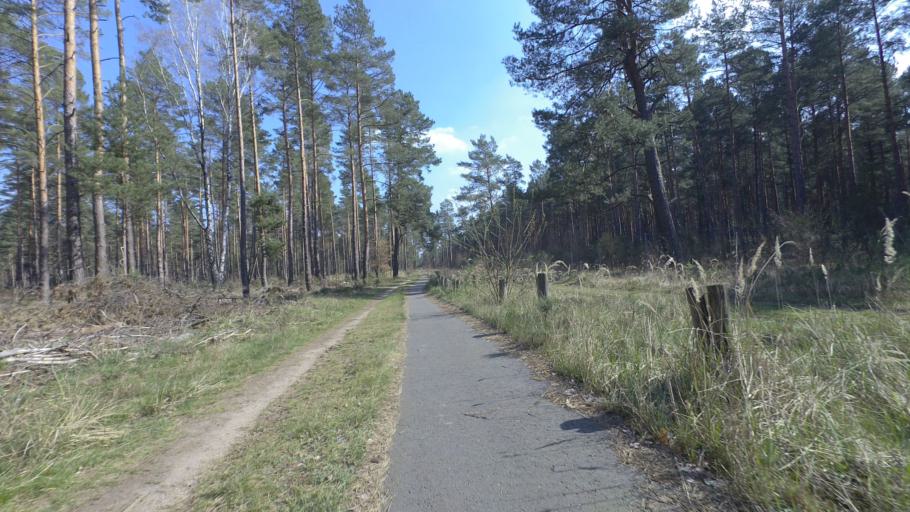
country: DE
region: Brandenburg
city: Mittenwalde
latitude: 52.1908
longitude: 13.5275
